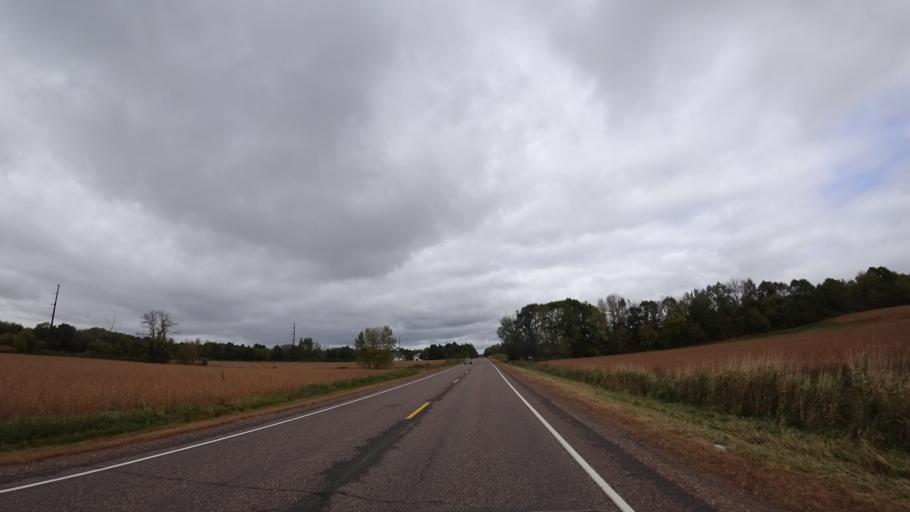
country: US
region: Wisconsin
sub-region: Chippewa County
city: Lake Wissota
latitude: 45.0156
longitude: -91.2867
